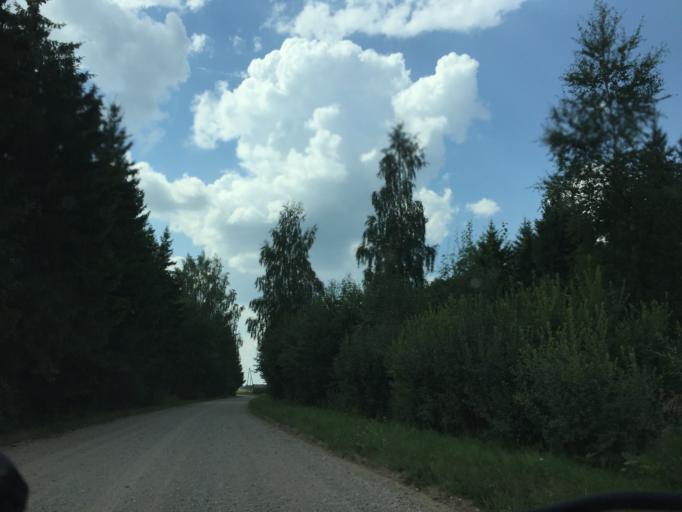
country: LT
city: Zagare
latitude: 56.3381
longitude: 23.0965
